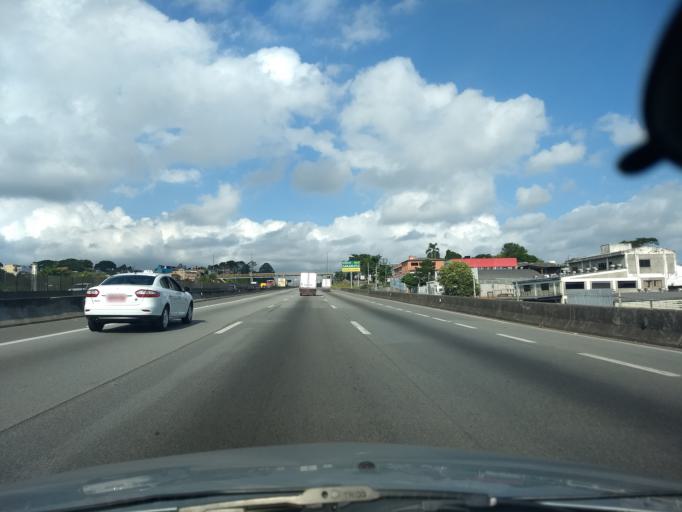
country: BR
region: Sao Paulo
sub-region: Itaquaquecetuba
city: Itaquaquecetuba
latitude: -23.4360
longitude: -46.4278
